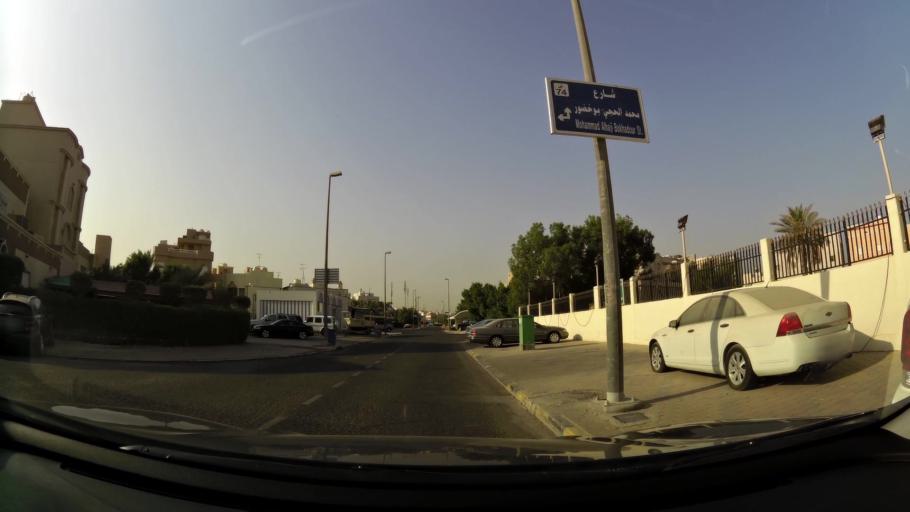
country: KW
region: Al Asimah
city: Ad Dasmah
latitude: 29.3643
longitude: 48.0080
